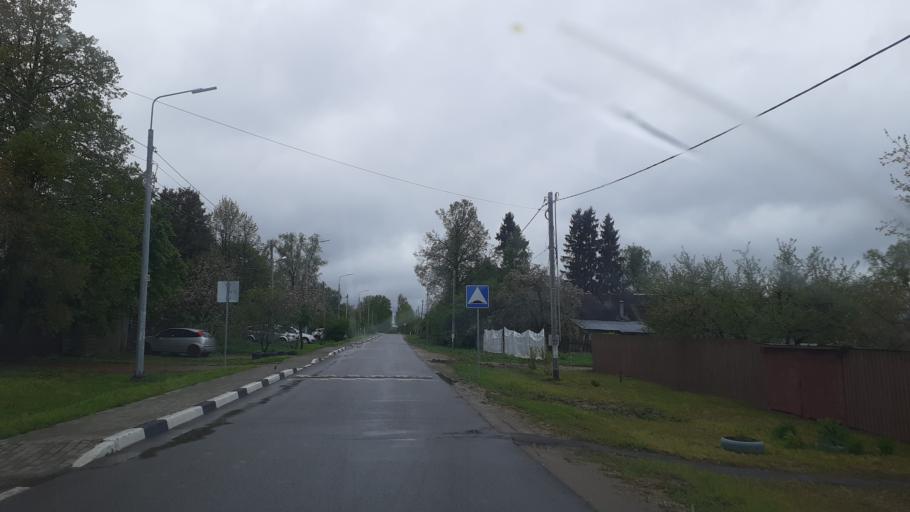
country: RU
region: Moskovskaya
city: Gorki Vtoryye
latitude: 55.7036
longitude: 37.2038
